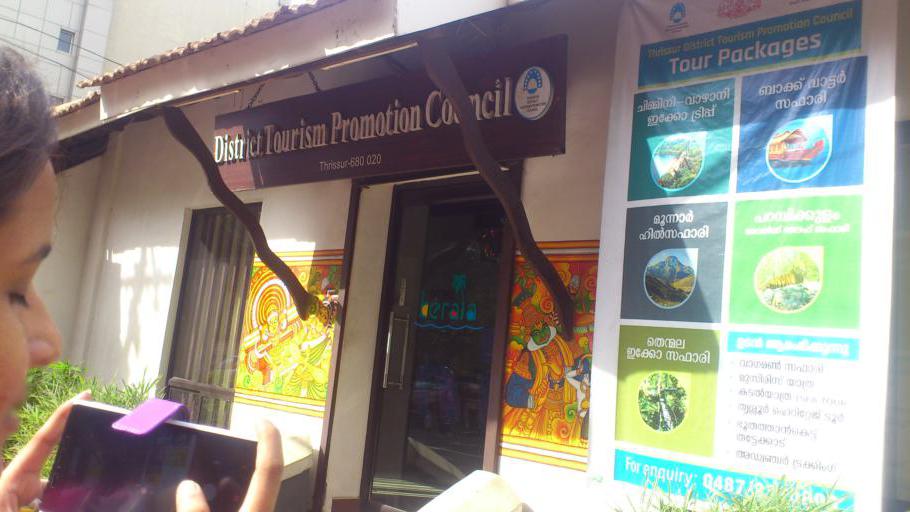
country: IN
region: Kerala
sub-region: Thrissur District
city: Trichur
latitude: 10.5295
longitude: 76.2179
